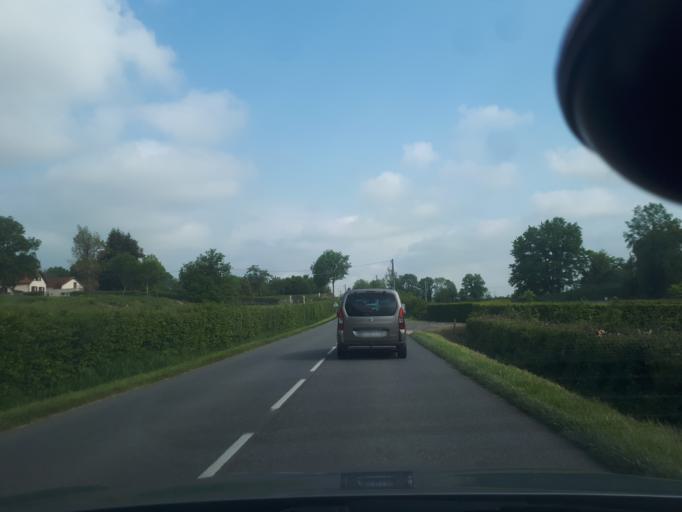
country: FR
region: Auvergne
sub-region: Departement de l'Allier
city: Lapalisse
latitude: 46.3271
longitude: 3.5846
